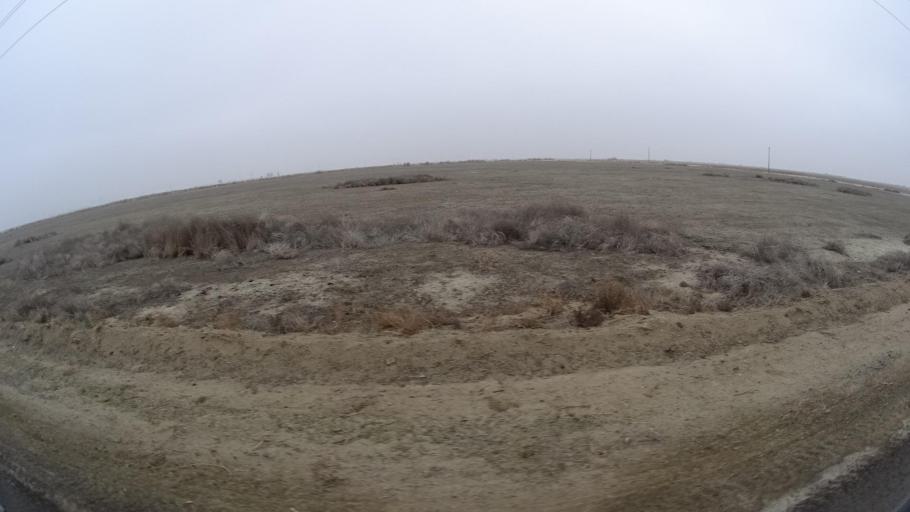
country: US
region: California
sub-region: Kern County
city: Lost Hills
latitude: 35.5928
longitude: -119.5805
